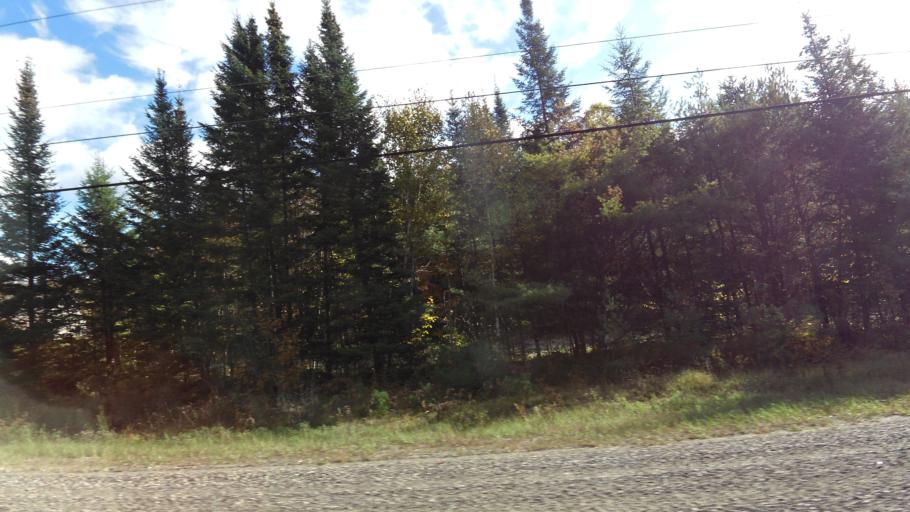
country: CA
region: Ontario
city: Deep River
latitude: 46.0674
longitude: -77.4750
